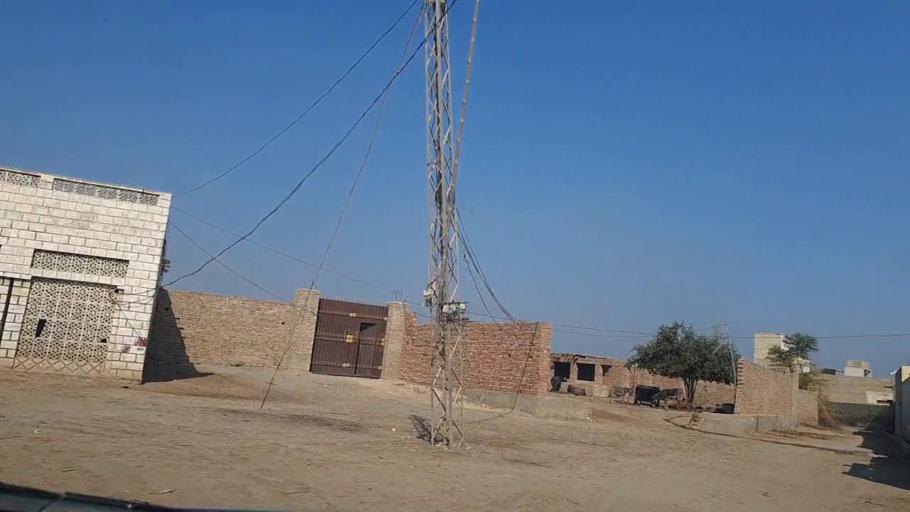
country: PK
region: Sindh
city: Sakrand
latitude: 26.0652
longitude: 68.3562
